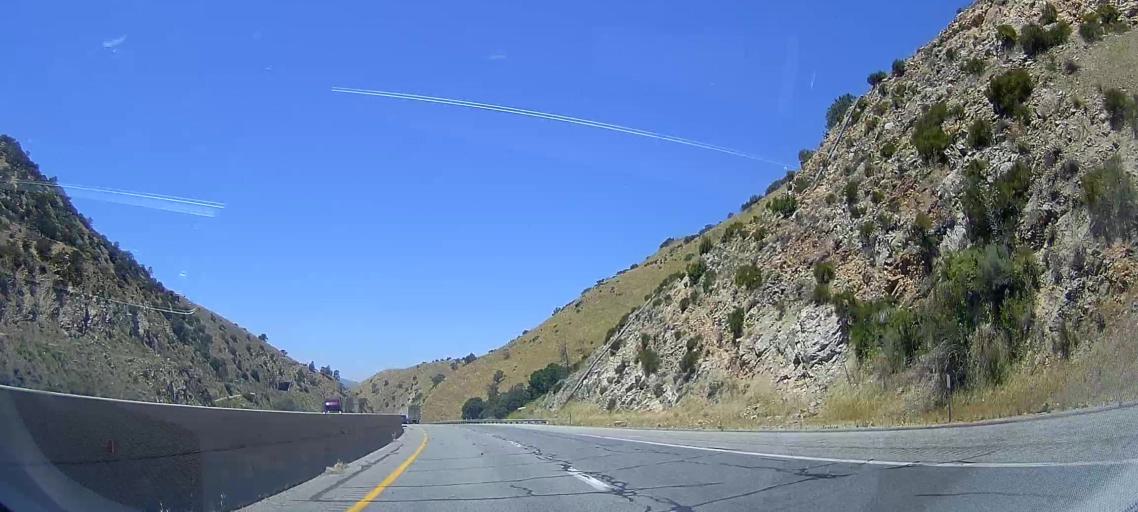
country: US
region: California
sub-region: Kern County
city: Golden Hills
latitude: 35.1780
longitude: -118.4827
